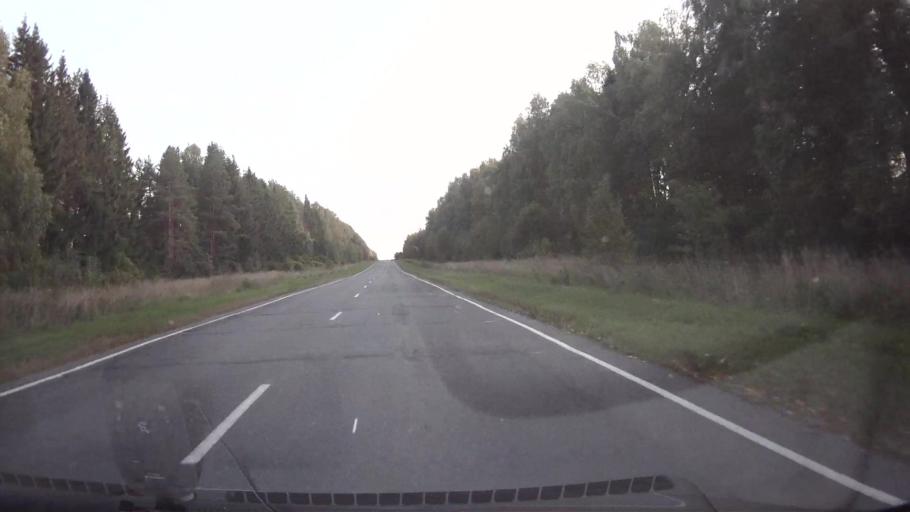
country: RU
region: Mariy-El
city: Kuzhener
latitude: 56.8773
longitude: 48.7538
